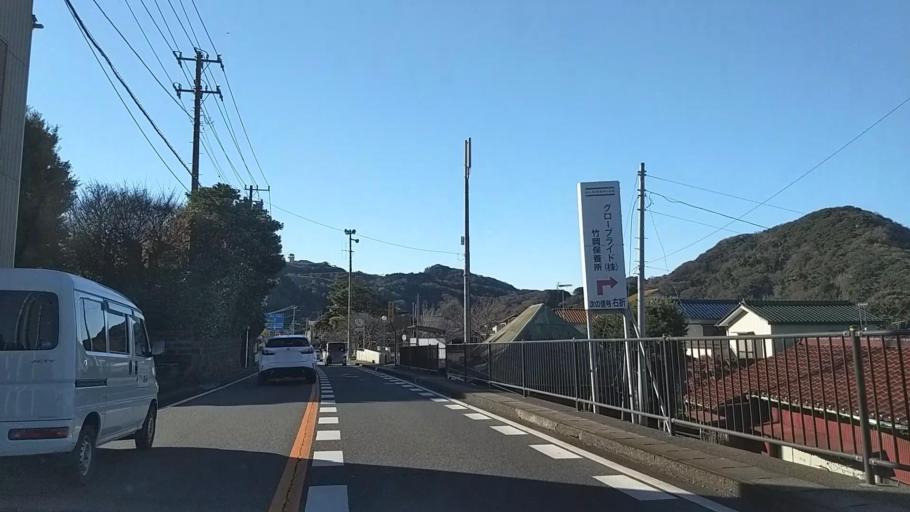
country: JP
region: Chiba
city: Futtsu
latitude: 35.2092
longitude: 139.8464
